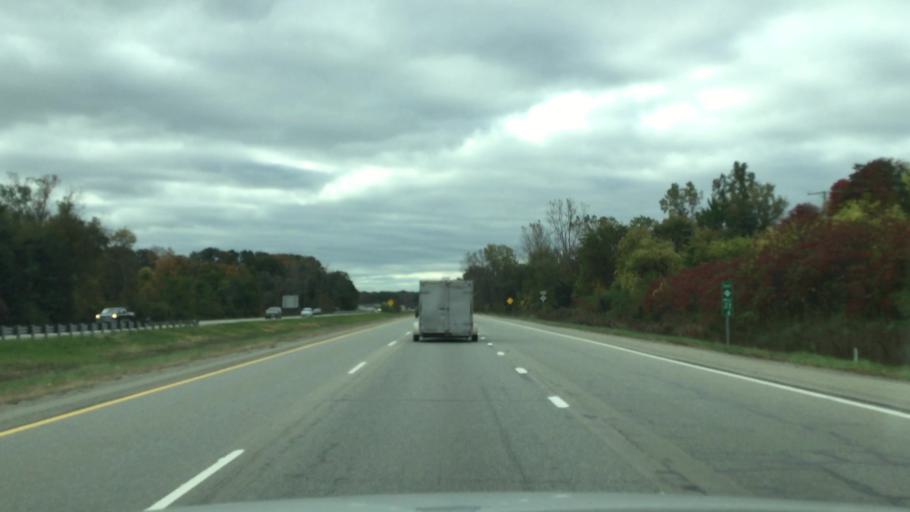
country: US
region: Michigan
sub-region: Macomb County
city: Shelby
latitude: 42.7095
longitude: -83.0262
